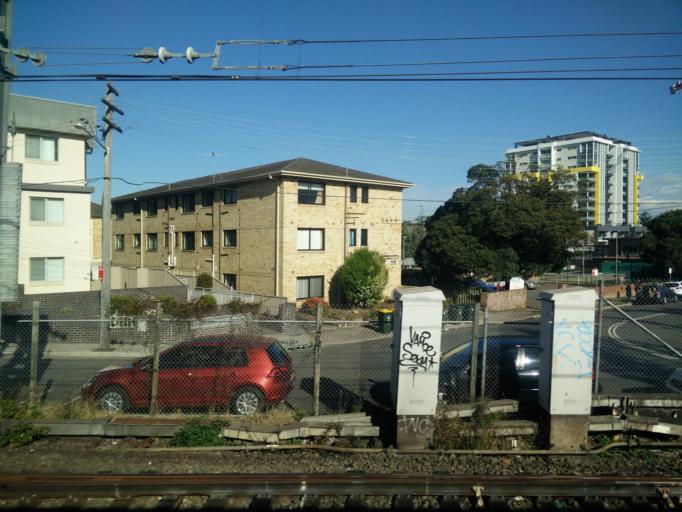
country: AU
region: New South Wales
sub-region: Strathfield
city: Homebush
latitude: -33.8741
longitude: 151.0969
